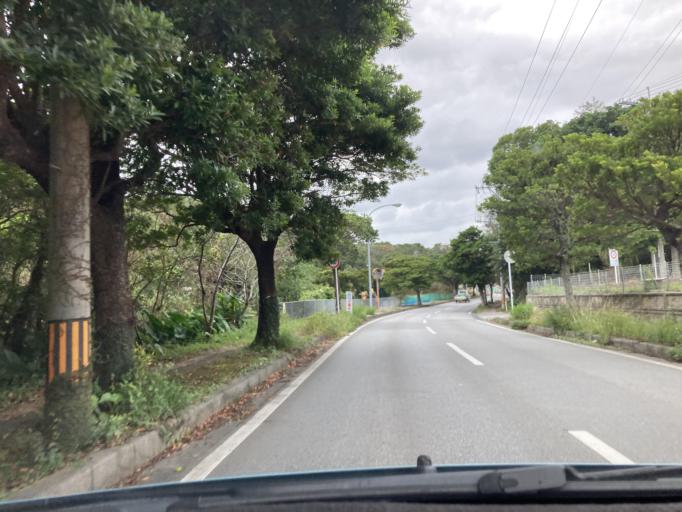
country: JP
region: Okinawa
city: Okinawa
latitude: 26.3450
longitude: 127.8083
